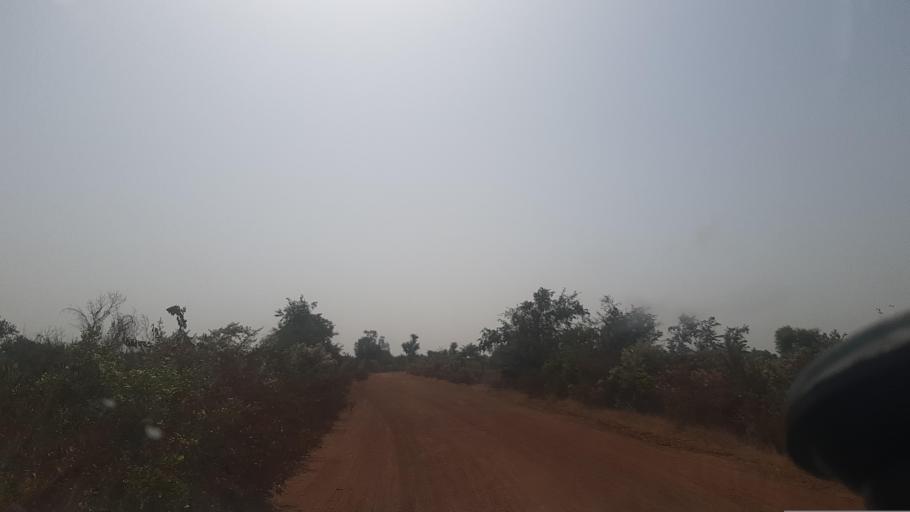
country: ML
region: Segou
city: Baroueli
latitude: 13.0600
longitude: -6.4724
